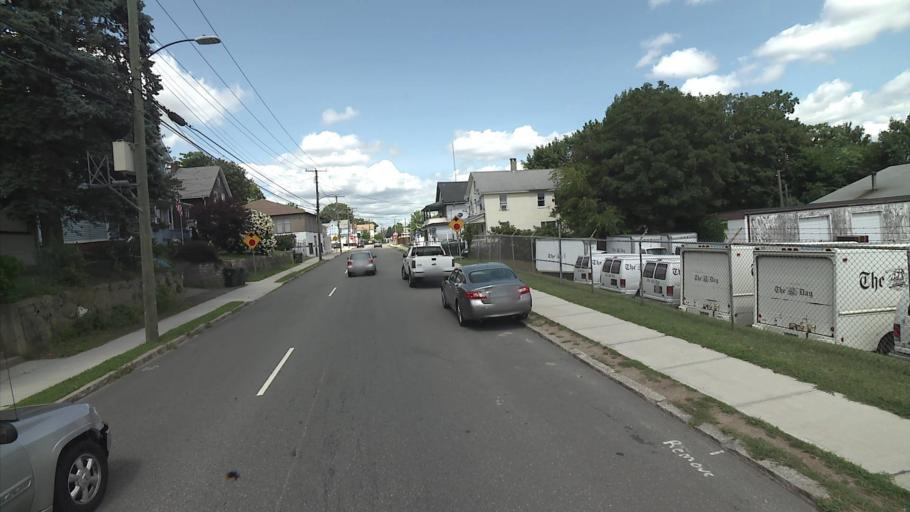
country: US
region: Connecticut
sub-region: New London County
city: New London
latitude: 41.3522
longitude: -72.1091
